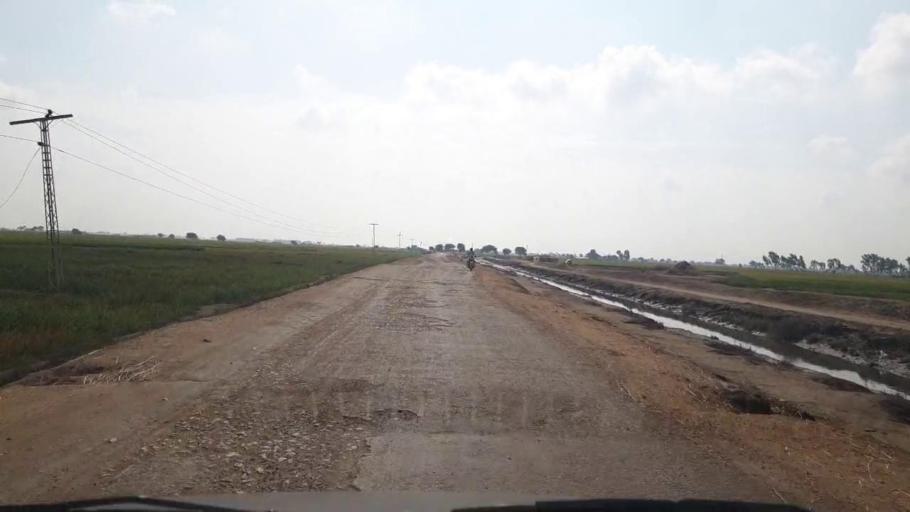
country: PK
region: Sindh
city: Kario
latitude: 24.6219
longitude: 68.5558
